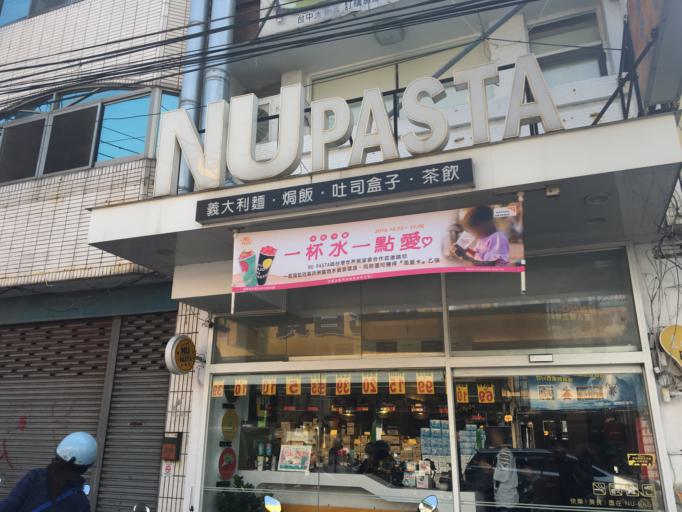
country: TW
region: Taiwan
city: Fengyuan
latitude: 24.3440
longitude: 120.6242
